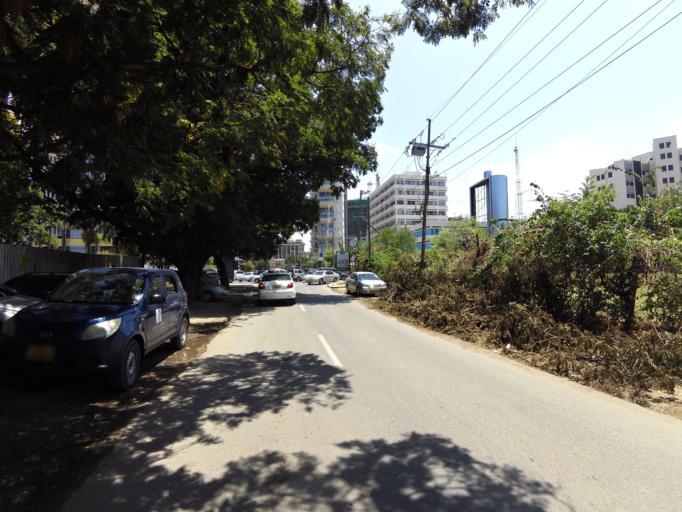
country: TZ
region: Dar es Salaam
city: Dar es Salaam
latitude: -6.8125
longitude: 39.2892
